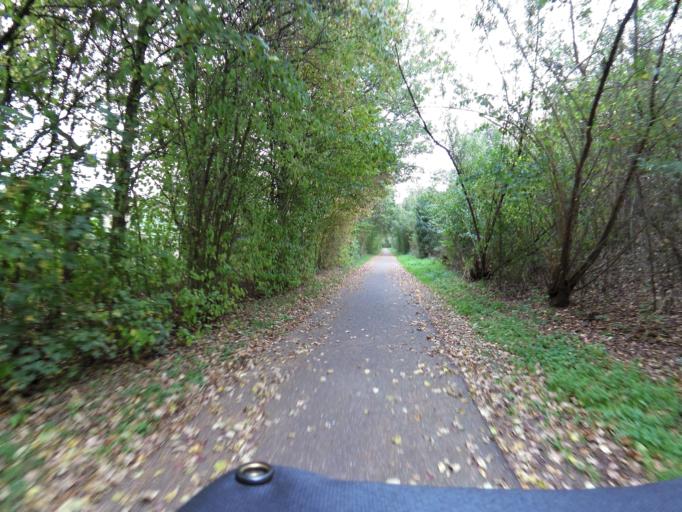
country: NL
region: North Brabant
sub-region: Gemeente Breda
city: Breda
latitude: 51.5258
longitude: 4.7557
